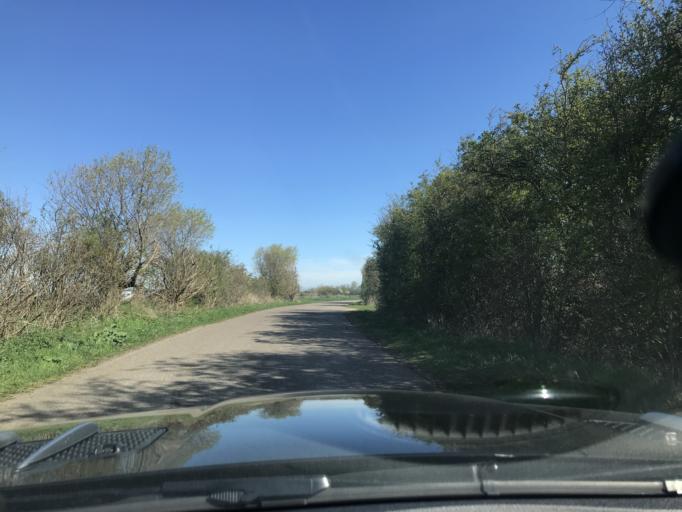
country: DE
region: Schleswig-Holstein
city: Grossenbrode
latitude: 54.4416
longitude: 11.0993
